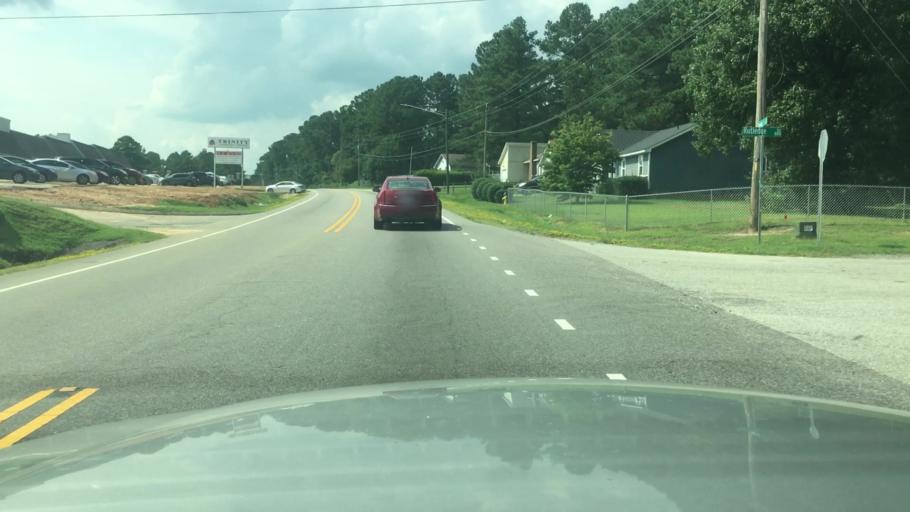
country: US
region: North Carolina
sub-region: Cumberland County
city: Fayetteville
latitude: 35.1111
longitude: -78.9036
